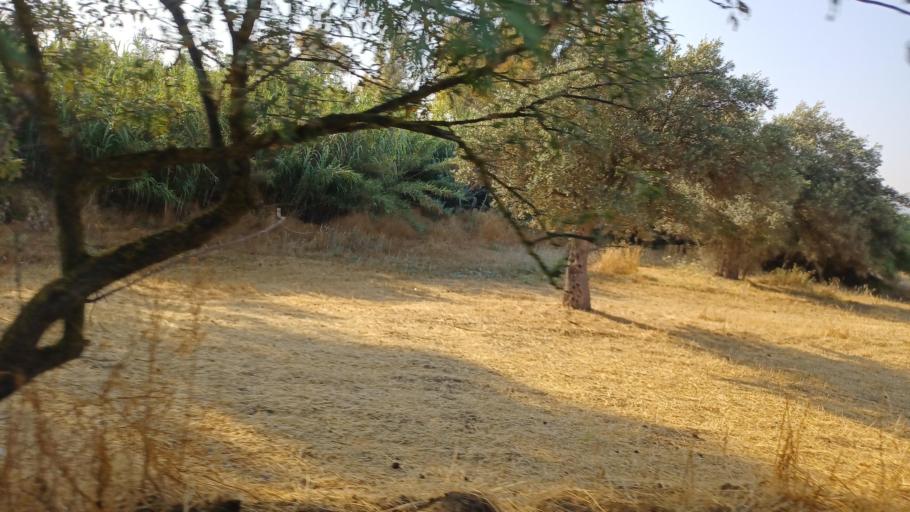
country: CY
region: Lefkosia
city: Lympia
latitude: 34.9829
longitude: 33.4385
